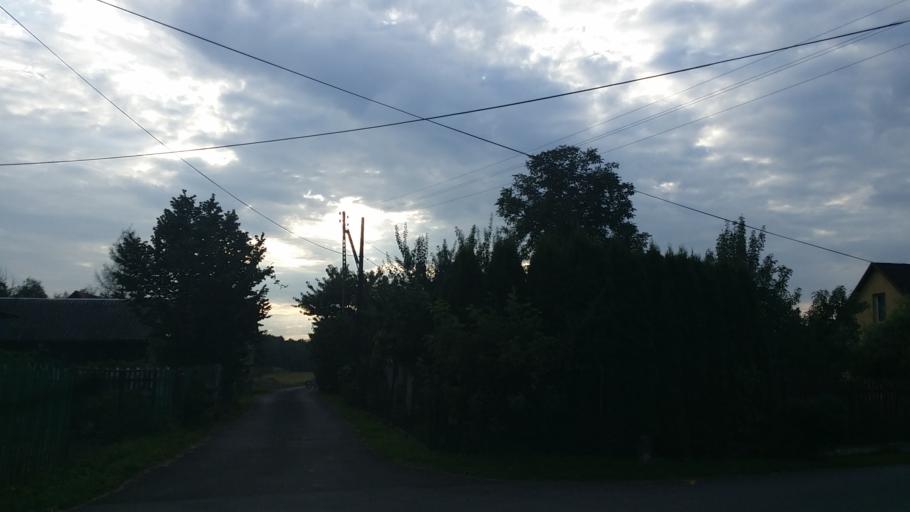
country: PL
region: Lesser Poland Voivodeship
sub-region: Powiat oswiecimski
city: Zator
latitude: 49.9911
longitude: 19.4216
